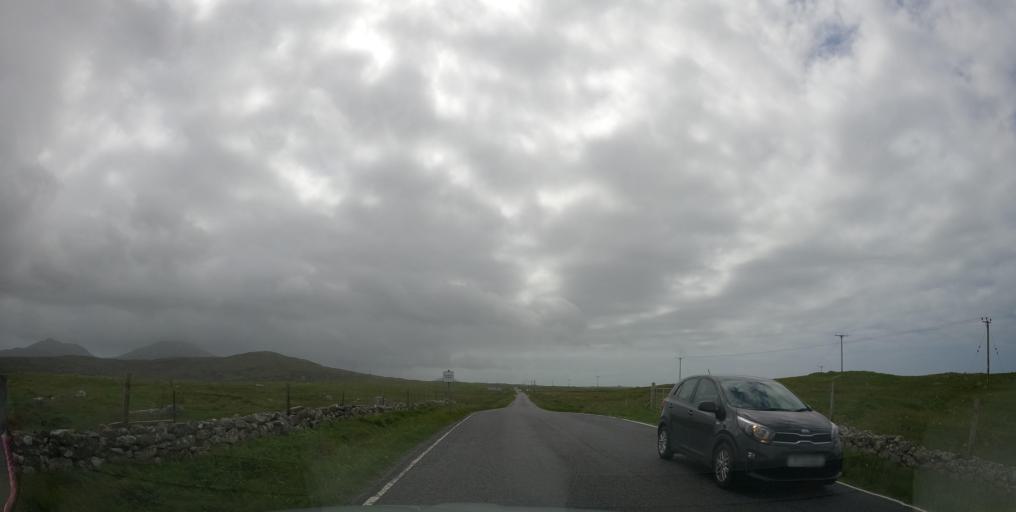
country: GB
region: Scotland
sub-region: Eilean Siar
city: Isle of South Uist
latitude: 57.3148
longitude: -7.3697
